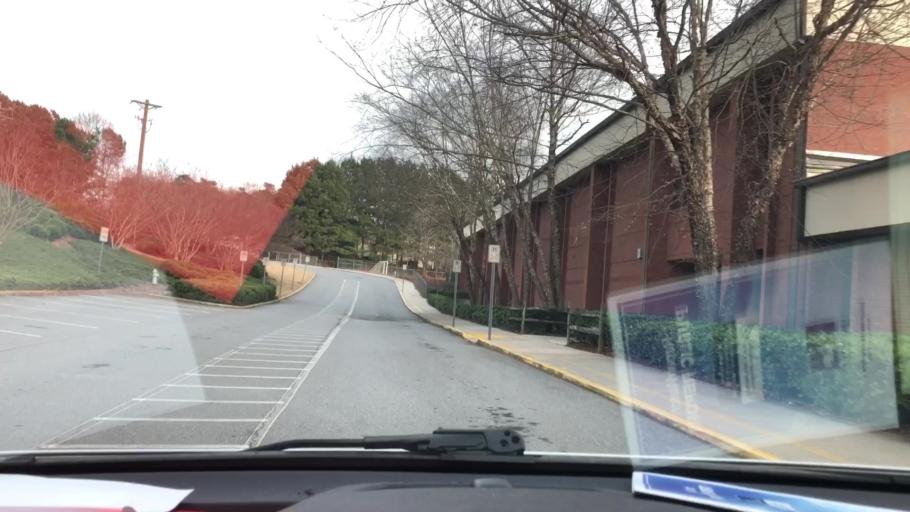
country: US
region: Georgia
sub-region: Gwinnett County
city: Duluth
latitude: 34.0186
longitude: -84.1476
